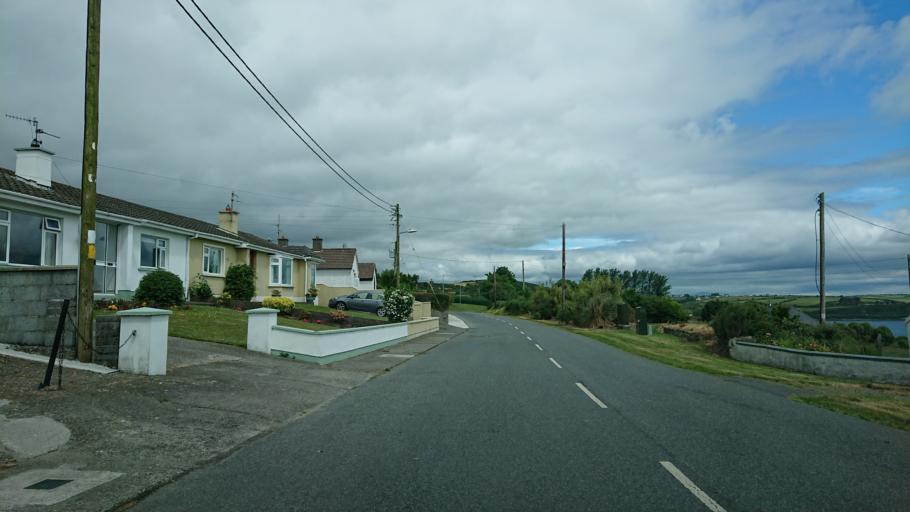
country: IE
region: Munster
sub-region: Waterford
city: Dunmore East
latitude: 52.2293
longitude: -6.9740
